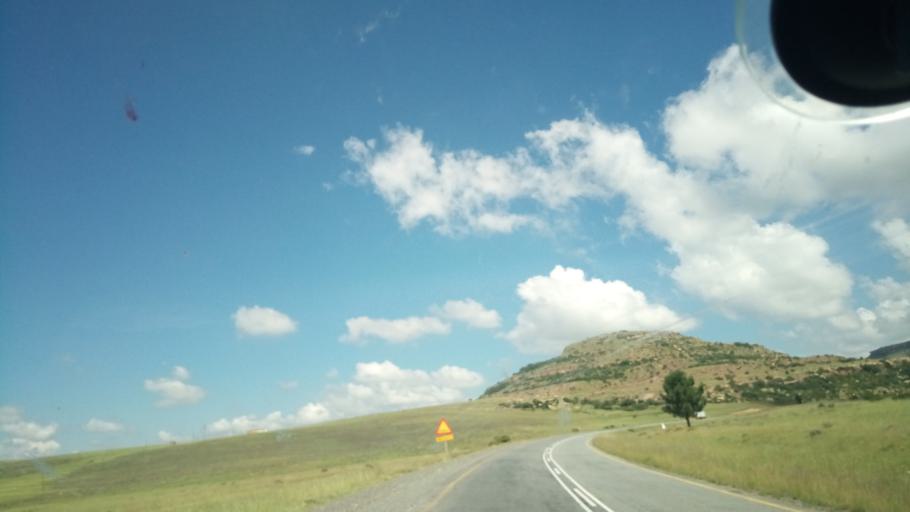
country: ZA
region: Orange Free State
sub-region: Thabo Mofutsanyana District Municipality
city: Ficksburg
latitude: -28.8933
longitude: 27.8488
